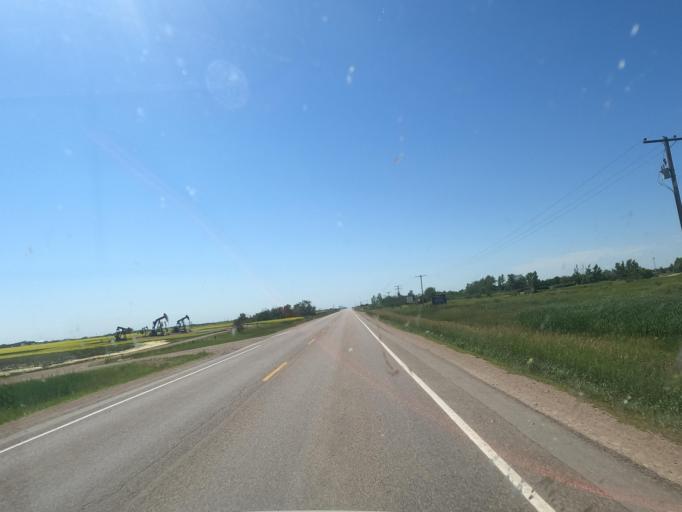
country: CA
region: Saskatchewan
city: Estevan
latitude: 49.6689
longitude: -103.0101
